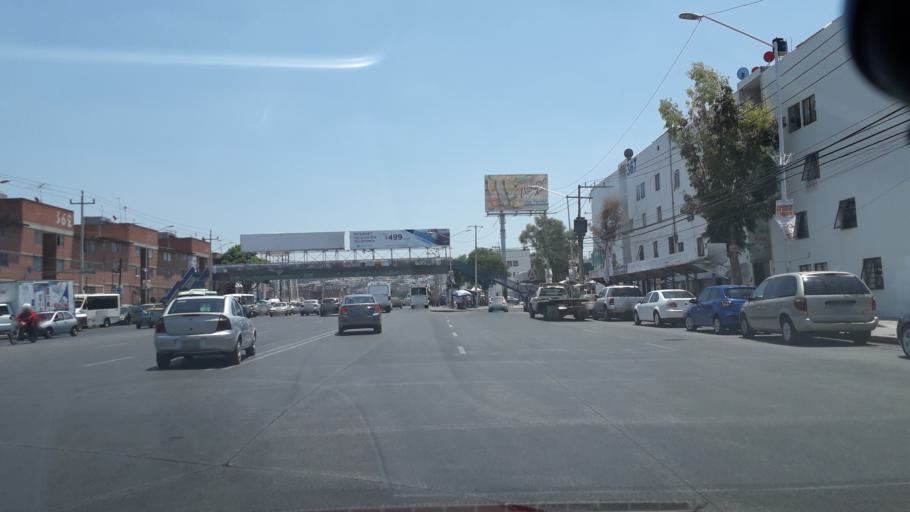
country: MX
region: Puebla
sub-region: Puebla
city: Galaxia la Calera
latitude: 19.0096
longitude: -98.1871
